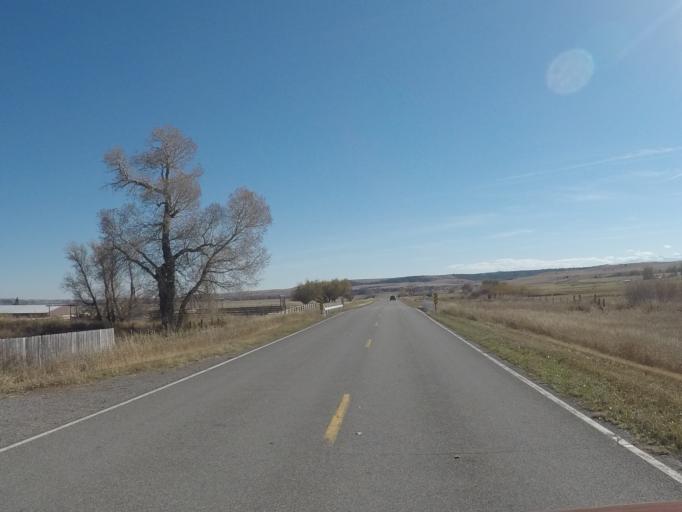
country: US
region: Montana
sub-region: Sweet Grass County
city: Big Timber
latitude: 45.8047
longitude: -109.8662
